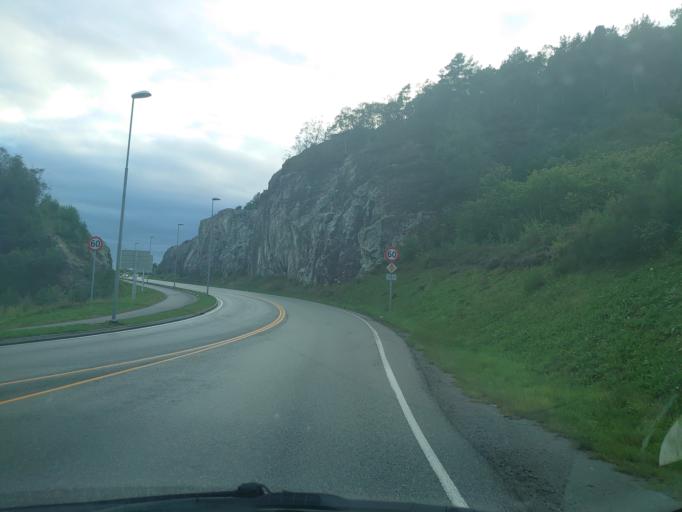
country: NO
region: Hordaland
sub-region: Lindas
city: Isdalsto
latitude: 60.5593
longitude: 5.2700
